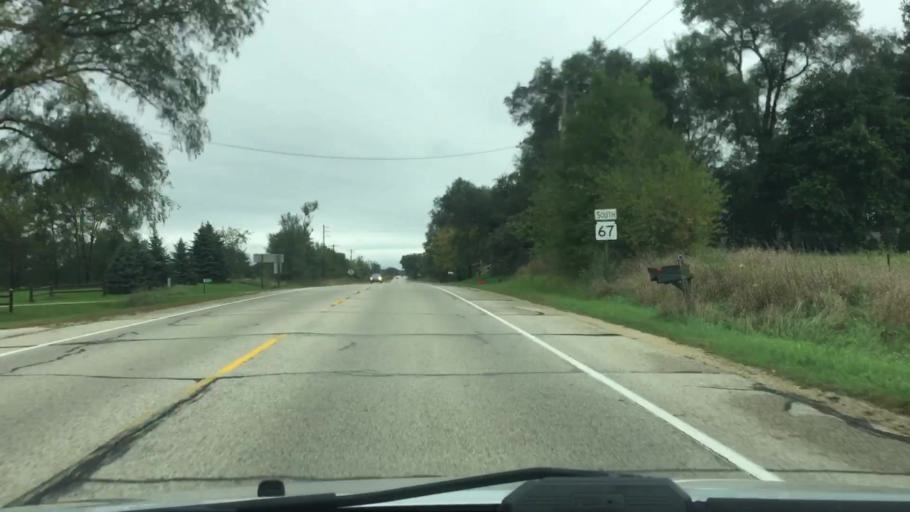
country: US
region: Wisconsin
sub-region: Jefferson County
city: Palmyra
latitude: 42.8356
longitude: -88.5429
